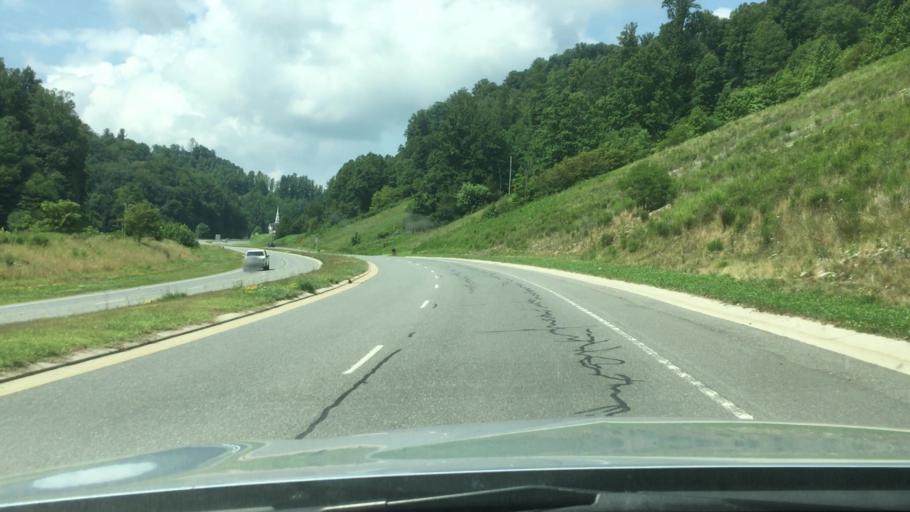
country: US
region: North Carolina
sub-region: Madison County
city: Mars Hill
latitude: 35.9142
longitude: -82.4642
